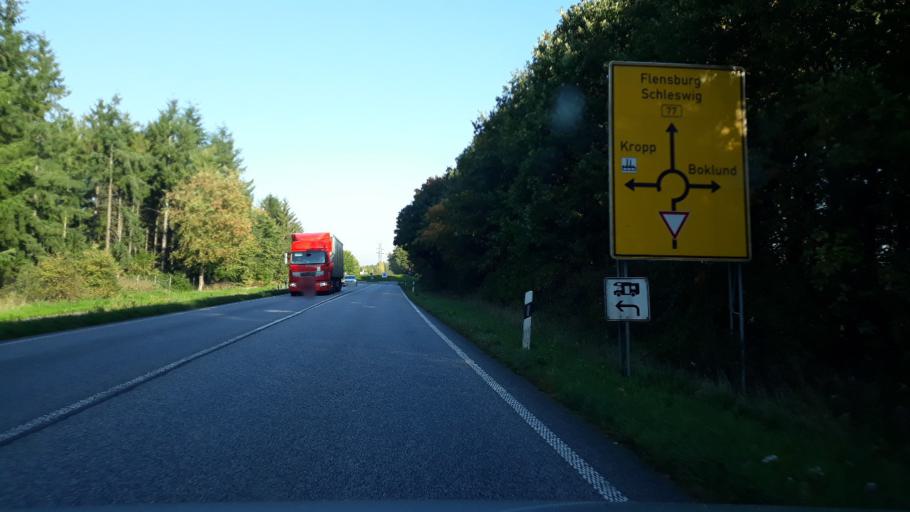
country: DE
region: Schleswig-Holstein
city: Kropp
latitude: 54.4107
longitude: 9.5317
